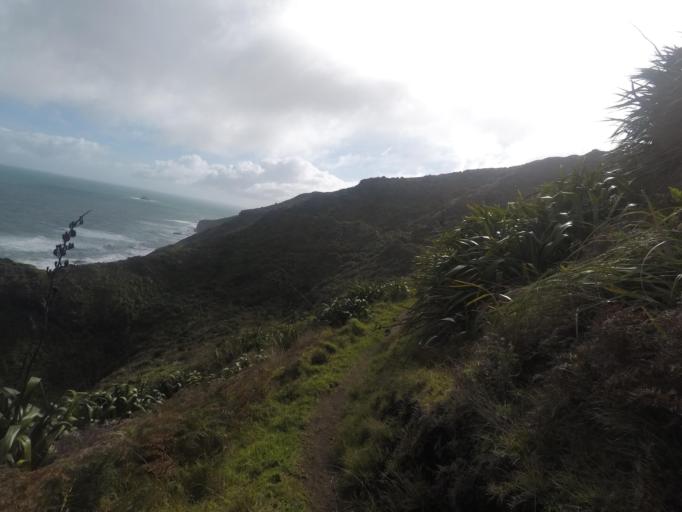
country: NZ
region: Auckland
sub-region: Auckland
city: Muriwai Beach
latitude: -36.8649
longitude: 174.4354
